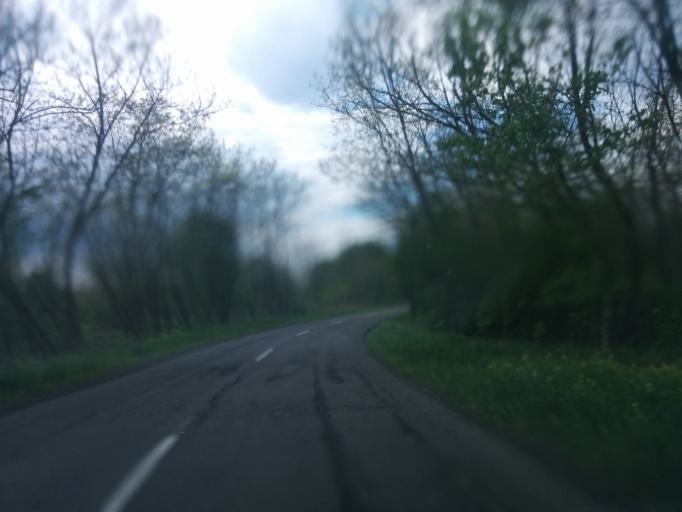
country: HU
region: Nograd
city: Palotas
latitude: 47.8276
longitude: 19.5710
